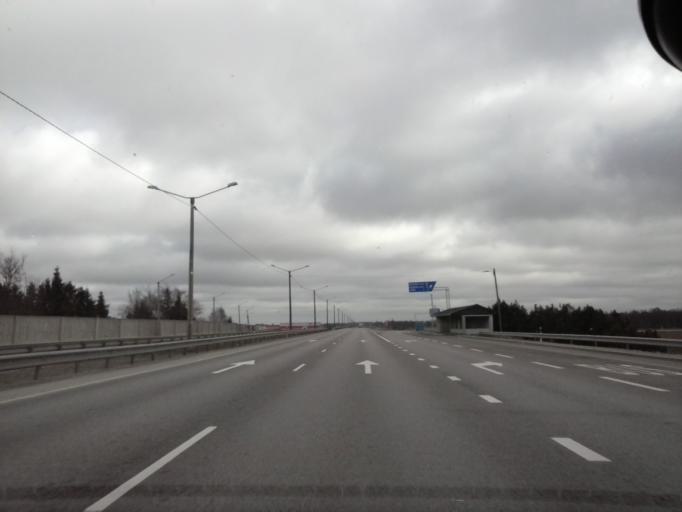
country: EE
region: Harju
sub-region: Rae vald
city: Jueri
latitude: 59.3574
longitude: 24.8759
